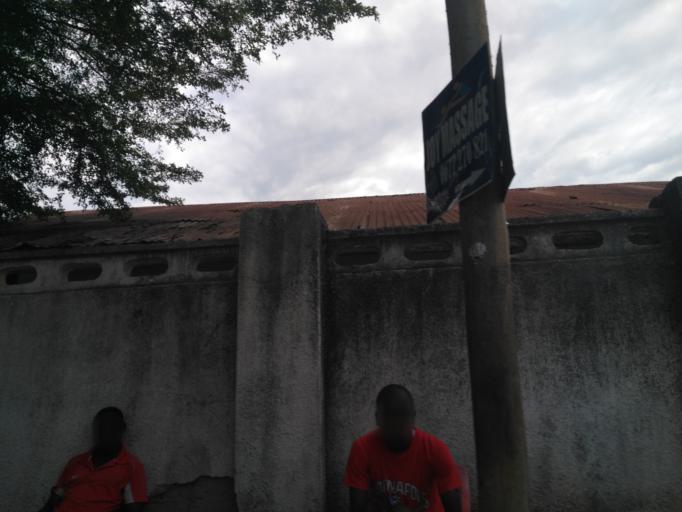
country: TZ
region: Dar es Salaam
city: Magomeni
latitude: -6.7528
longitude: 39.2421
